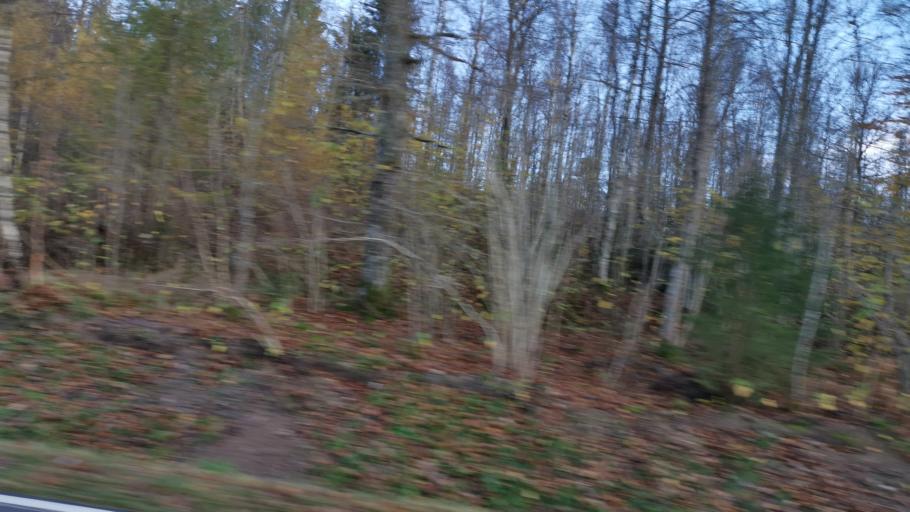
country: SE
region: Vaestra Goetaland
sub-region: Munkedals Kommun
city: Munkedal
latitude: 58.4866
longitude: 11.7061
